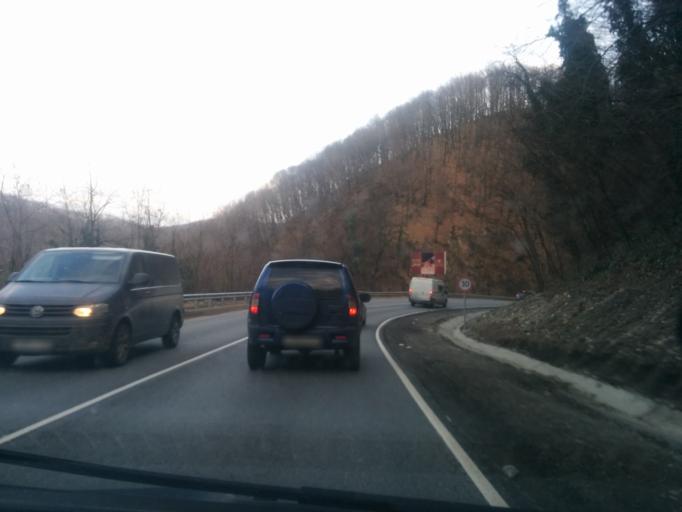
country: RU
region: Krasnodarskiy
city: Agoy
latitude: 44.1177
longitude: 39.0491
